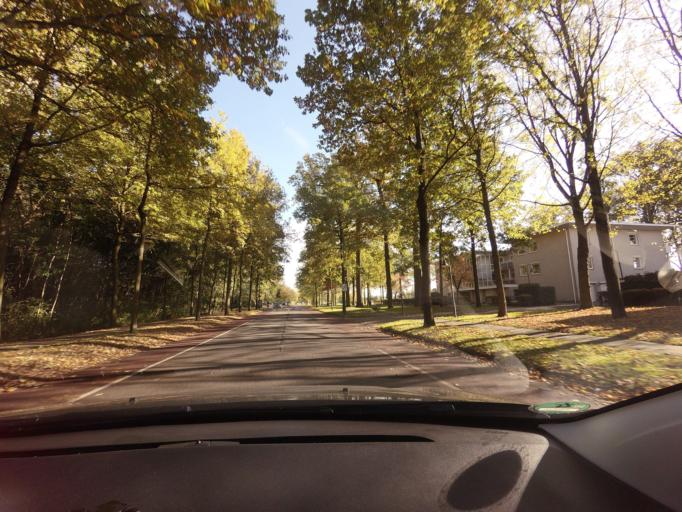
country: NL
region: Utrecht
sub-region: Stichtse Vecht
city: Spechtenkamp
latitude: 52.1051
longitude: 5.0176
